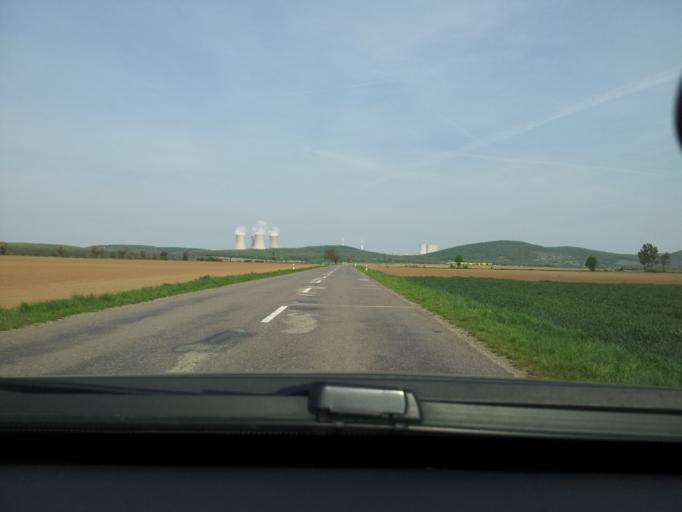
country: SK
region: Nitriansky
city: Tlmace
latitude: 48.2270
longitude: 18.4932
